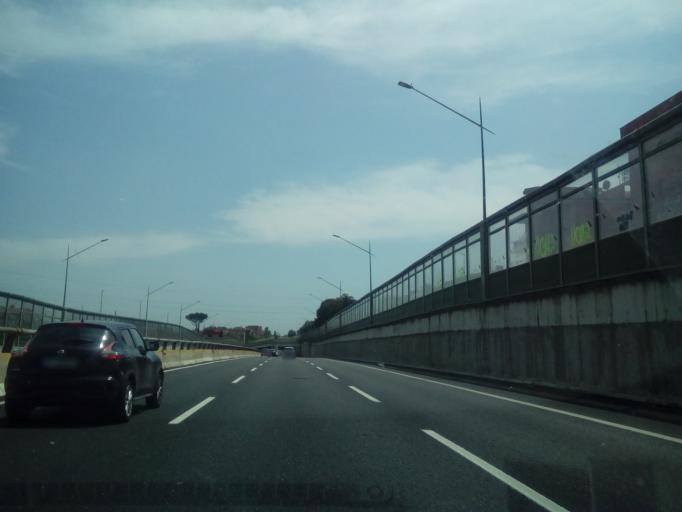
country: IT
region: Latium
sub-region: Citta metropolitana di Roma Capitale
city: Valle Santa
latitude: 41.9522
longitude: 12.3830
